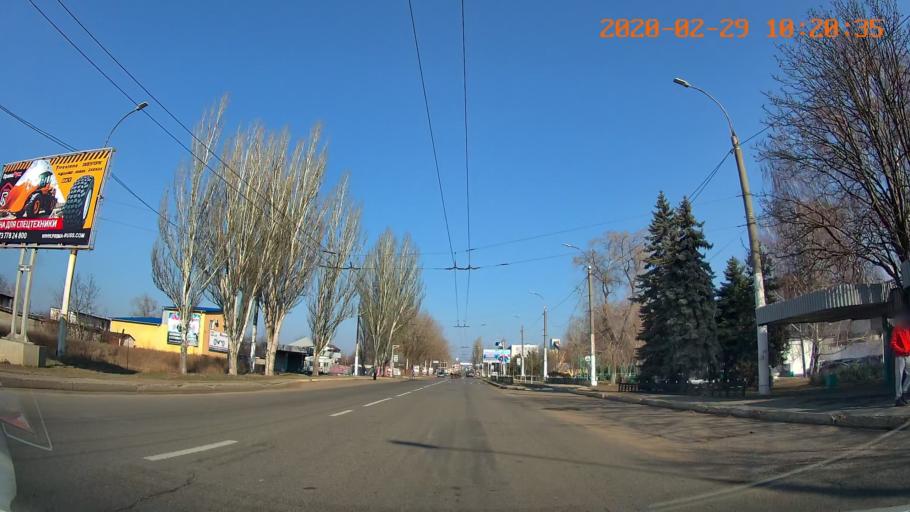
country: MD
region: Telenesti
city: Tiraspolul Nou
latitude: 46.8615
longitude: 29.6103
